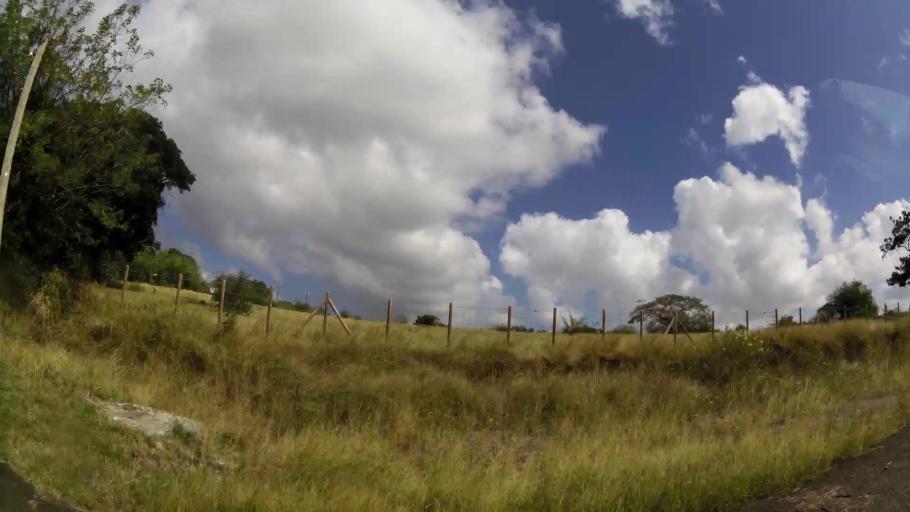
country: MQ
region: Martinique
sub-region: Martinique
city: Fort-de-France
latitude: 14.6376
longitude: -61.1337
